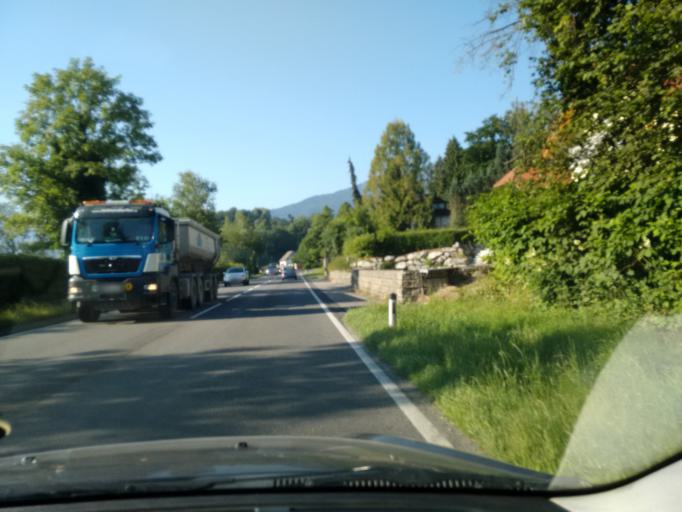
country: AT
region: Upper Austria
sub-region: Politischer Bezirk Gmunden
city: Altmunster
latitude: 47.8754
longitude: 13.7759
